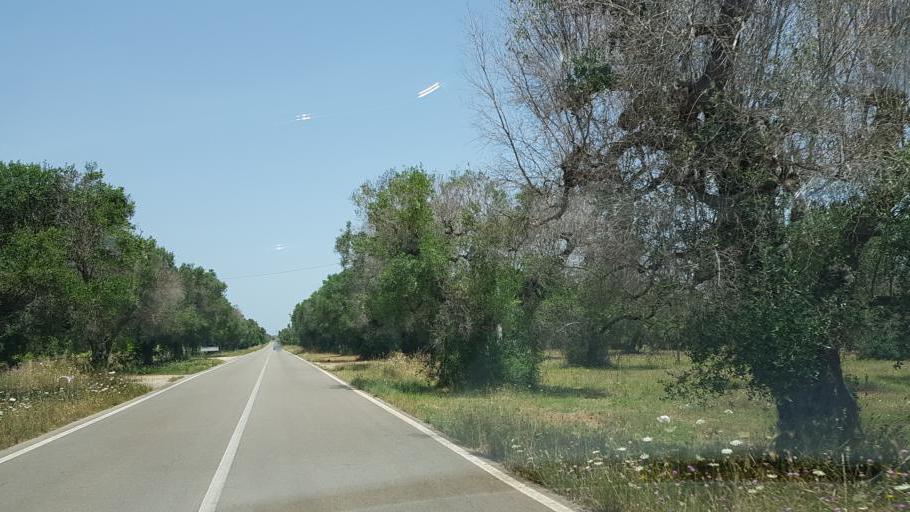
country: IT
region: Apulia
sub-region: Provincia di Lecce
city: Veglie
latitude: 40.3186
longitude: 17.9231
